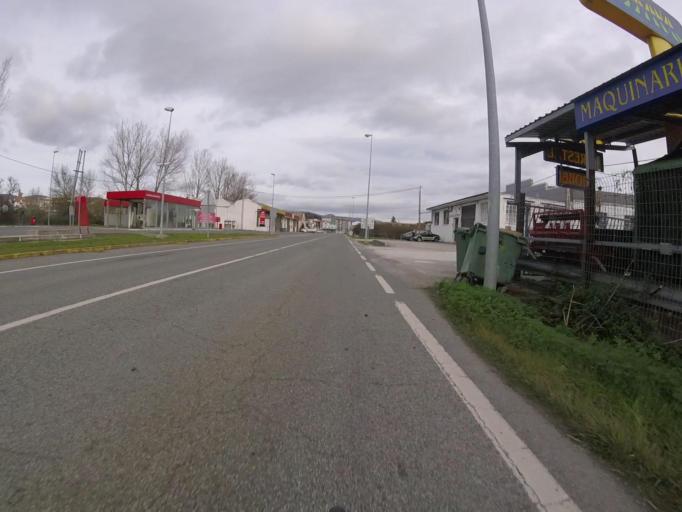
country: ES
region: Navarre
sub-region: Provincia de Navarra
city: Altsasu
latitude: 42.8899
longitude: -2.1688
